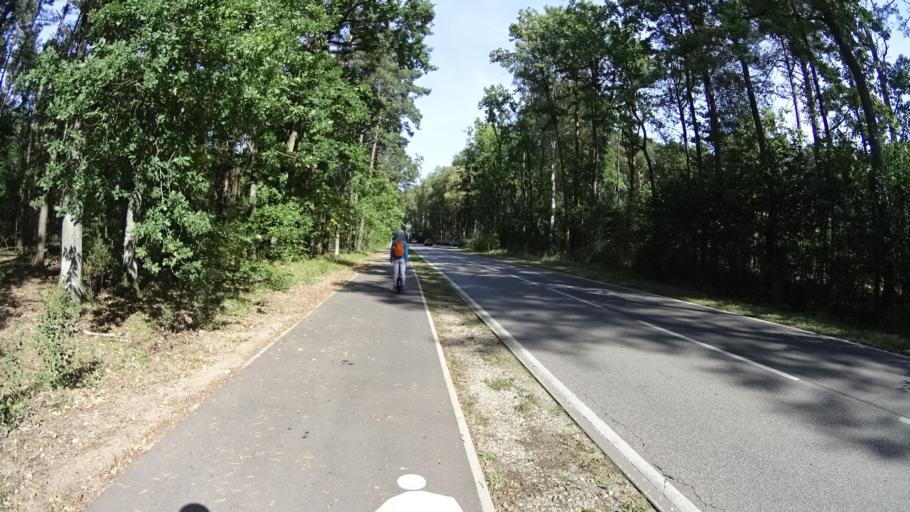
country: PL
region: Masovian Voivodeship
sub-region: Powiat legionowski
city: Bialobrzegi
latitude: 52.4535
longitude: 21.0707
